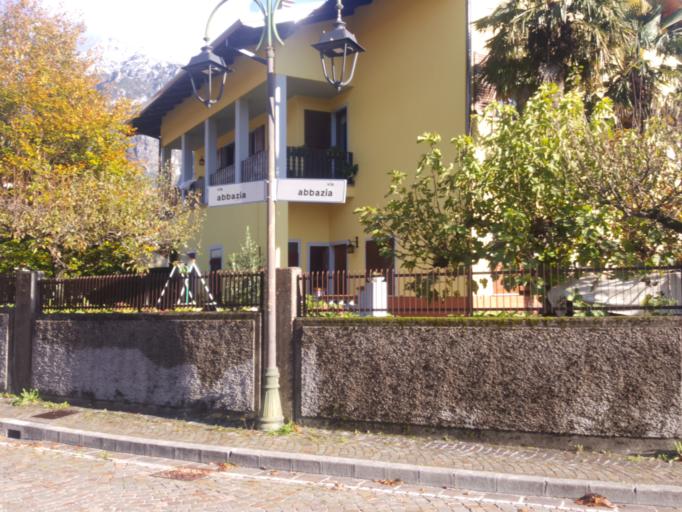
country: IT
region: Friuli Venezia Giulia
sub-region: Provincia di Udine
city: Moggio di Sotto
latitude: 46.4063
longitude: 13.1892
